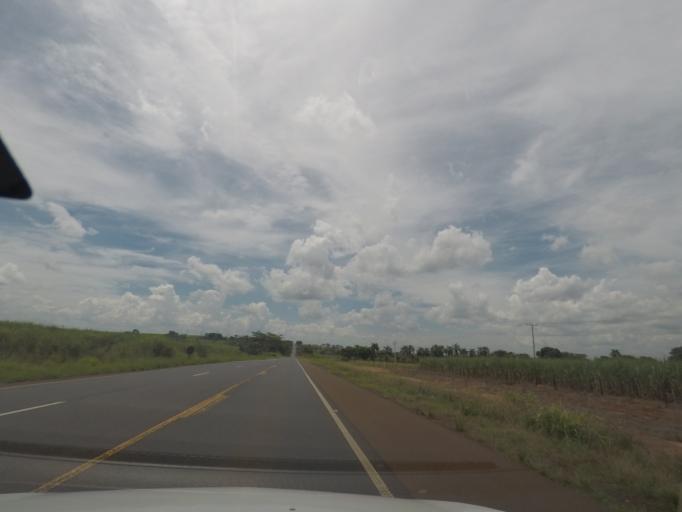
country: BR
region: Sao Paulo
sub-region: Barretos
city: Barretos
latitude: -20.4099
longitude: -48.6339
